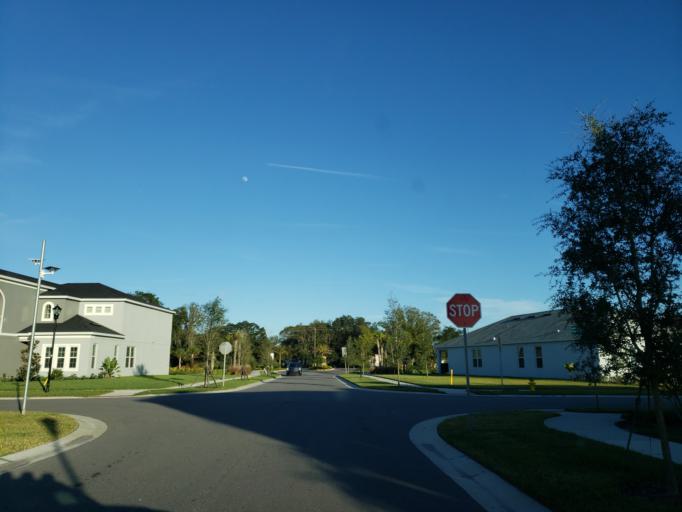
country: US
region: Florida
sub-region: Hillsborough County
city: Fish Hawk
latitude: 27.8385
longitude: -82.2006
